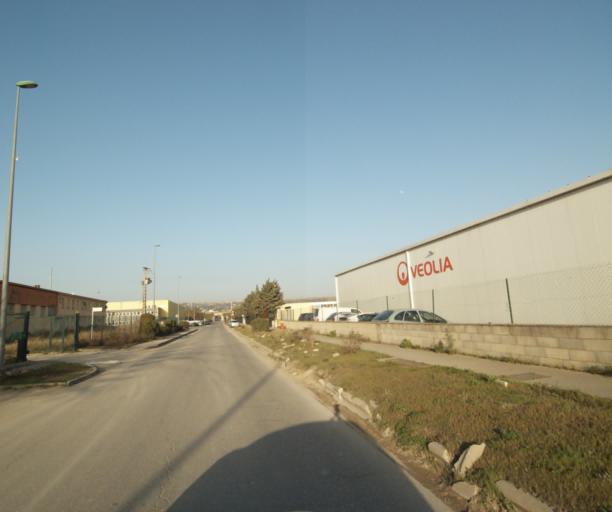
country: FR
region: Provence-Alpes-Cote d'Azur
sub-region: Departement des Bouches-du-Rhone
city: Saint-Victoret
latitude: 43.4251
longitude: 5.2437
